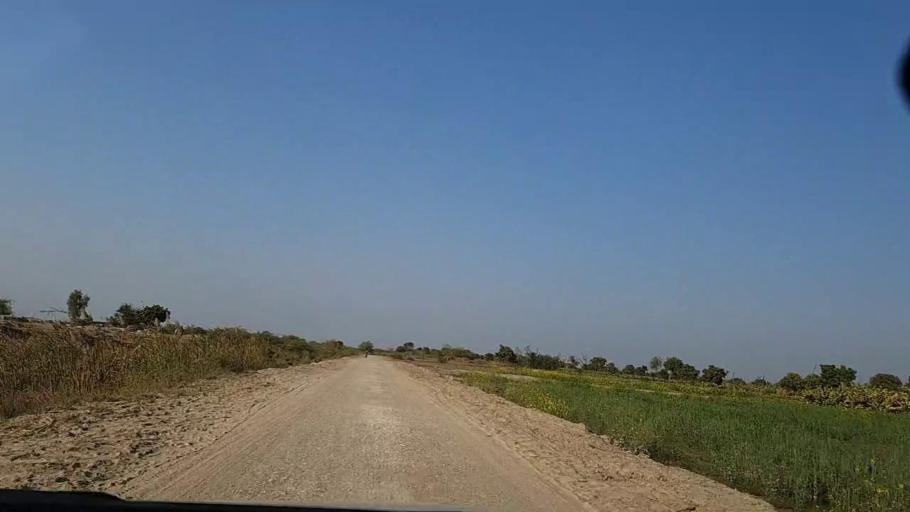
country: PK
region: Sindh
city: Mirwah Gorchani
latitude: 25.2314
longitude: 68.9813
